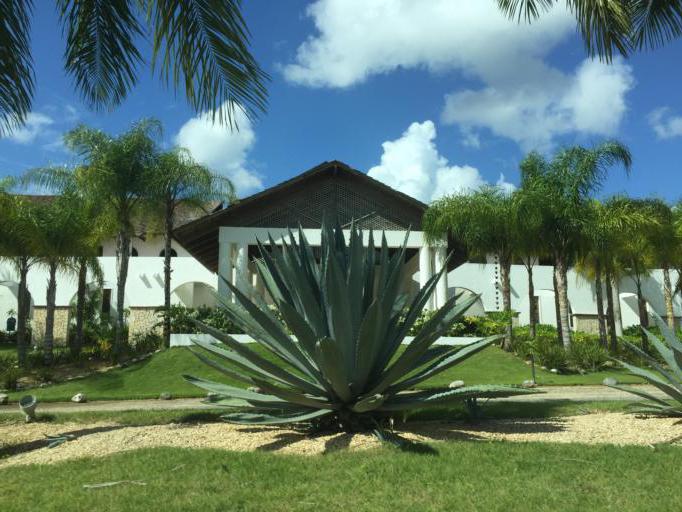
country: DO
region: Santo Domingo
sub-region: Santo Domingo
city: Boca Chica
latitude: 18.4674
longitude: -69.6538
